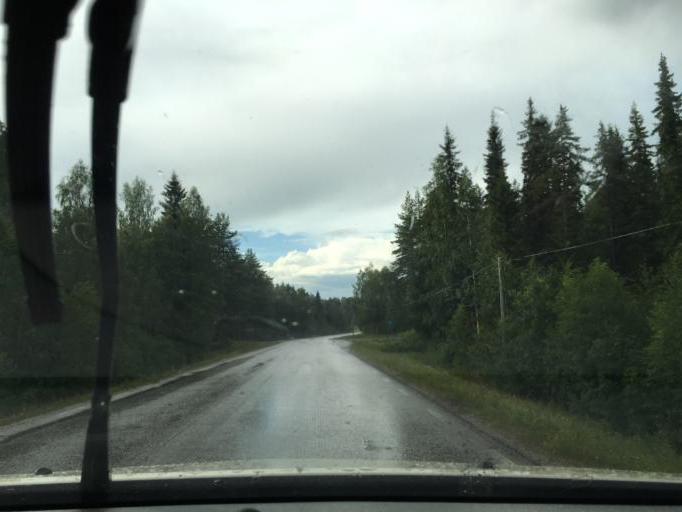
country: SE
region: Norrbotten
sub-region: Kalix Kommun
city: Toere
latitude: 65.9438
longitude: 22.8919
